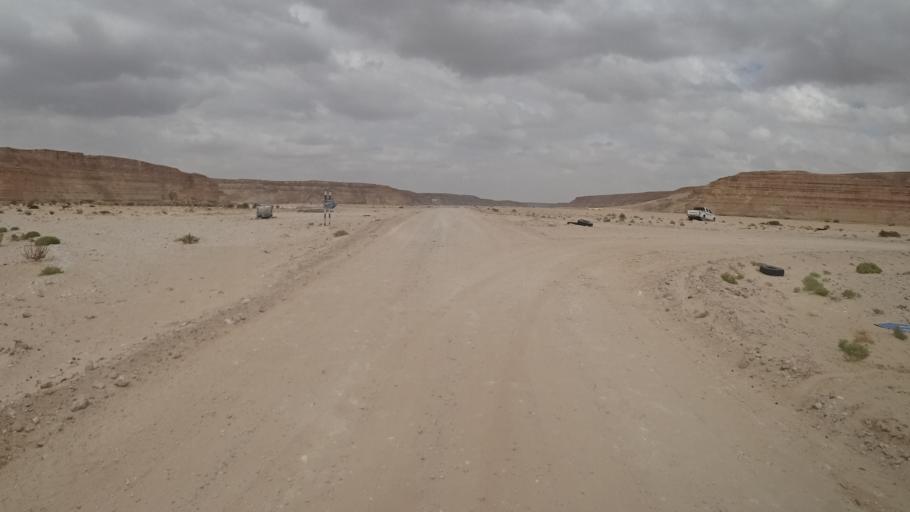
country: YE
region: Al Mahrah
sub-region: Shahan
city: Shihan as Sufla
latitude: 17.4723
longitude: 53.0004
